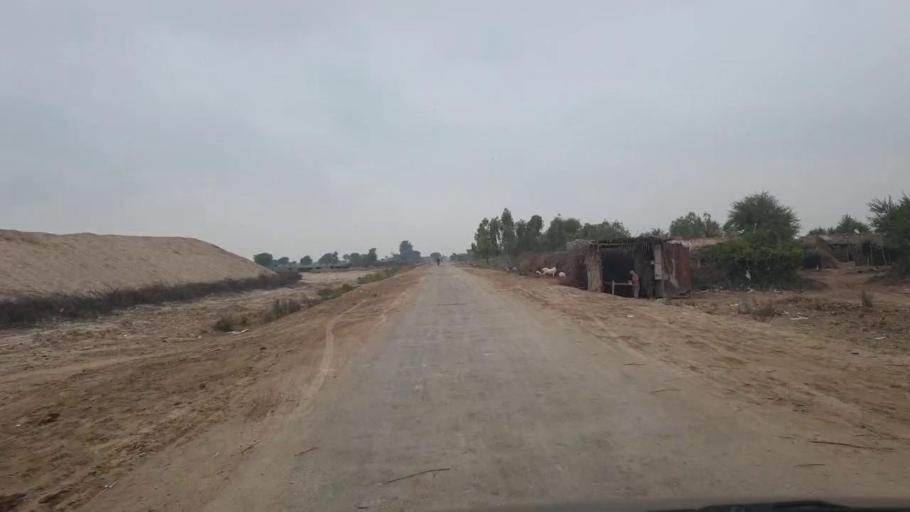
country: PK
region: Sindh
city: Shahdadpur
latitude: 25.9604
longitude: 68.7226
